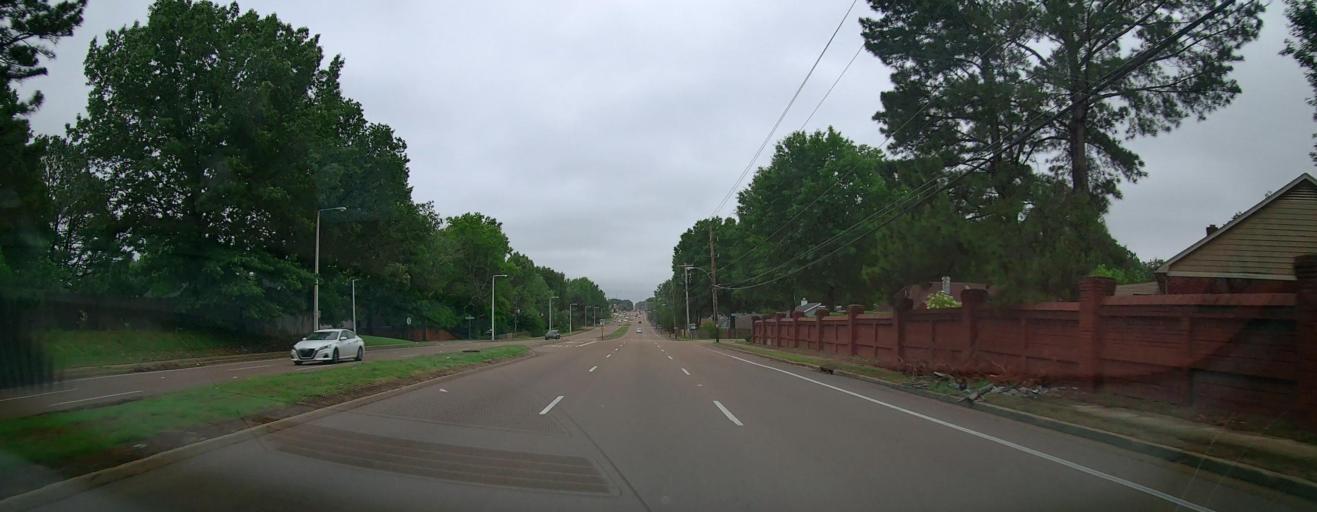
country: US
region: Tennessee
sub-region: Shelby County
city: Germantown
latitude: 35.0289
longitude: -89.8314
